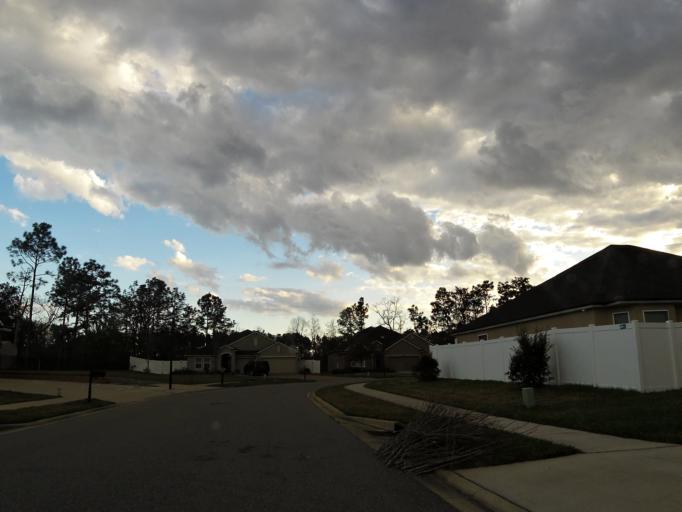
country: US
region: Florida
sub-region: Saint Johns County
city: Fruit Cove
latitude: 30.1711
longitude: -81.5672
